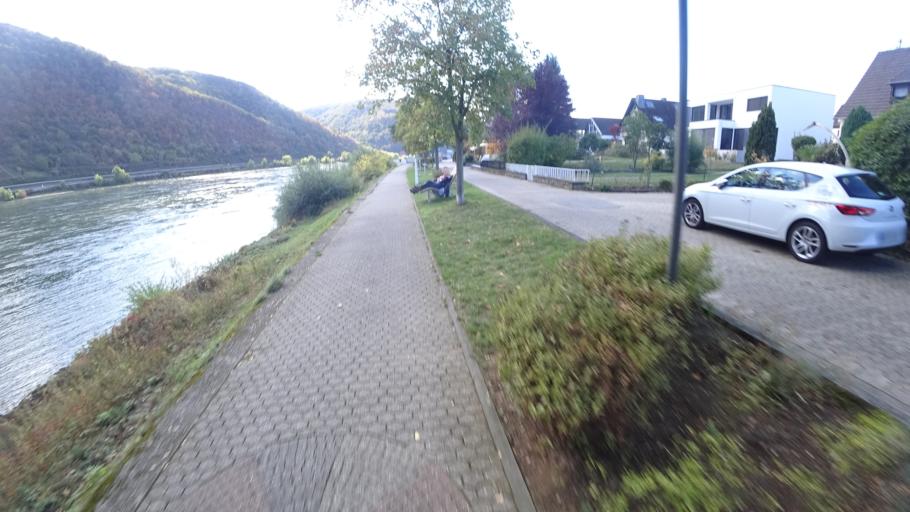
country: DE
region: Rheinland-Pfalz
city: Spay
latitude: 50.2588
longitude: 7.6501
